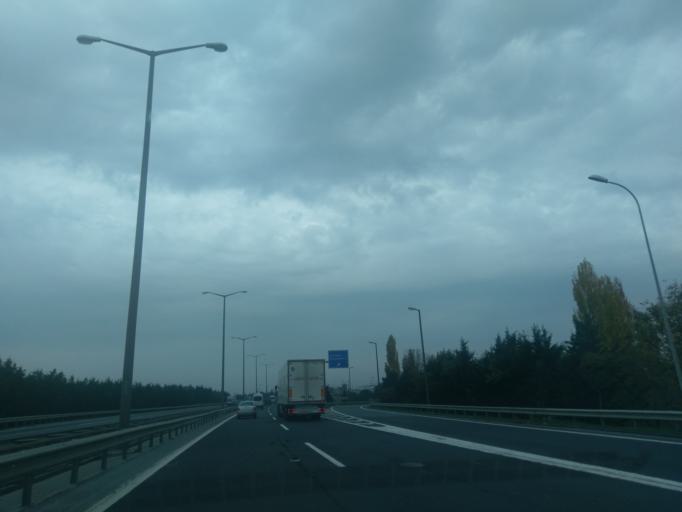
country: TR
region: Istanbul
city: Muratbey
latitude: 41.0858
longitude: 28.5081
